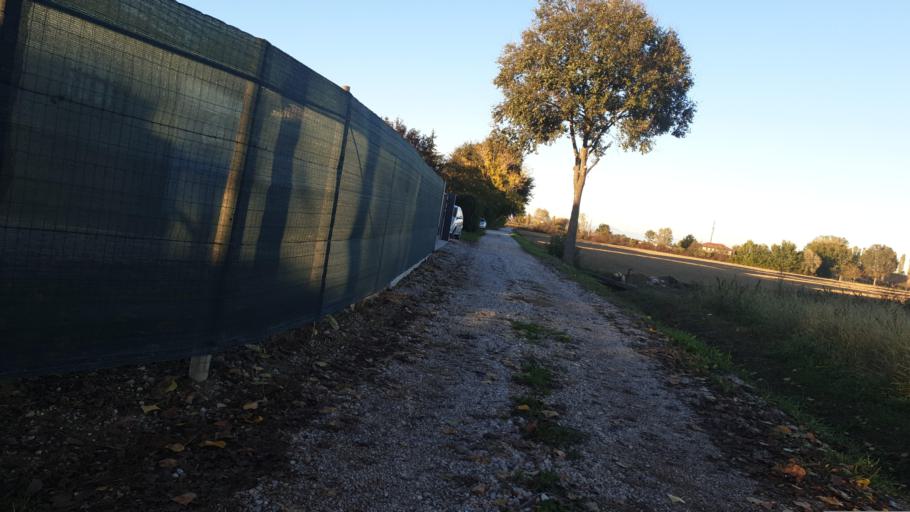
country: IT
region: Veneto
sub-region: Provincia di Venezia
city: Marano
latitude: 45.4454
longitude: 12.1001
